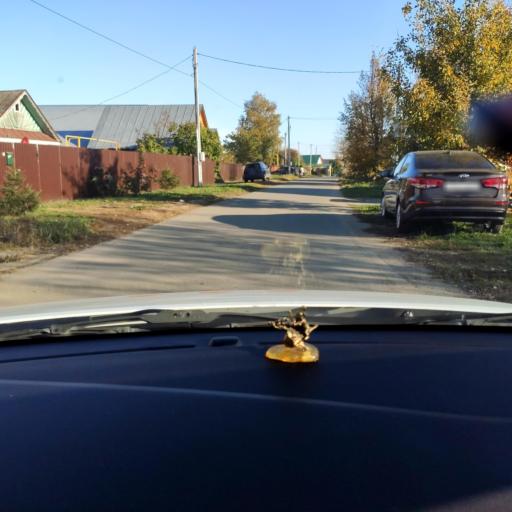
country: RU
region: Tatarstan
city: Stolbishchi
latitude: 55.6252
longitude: 49.1514
